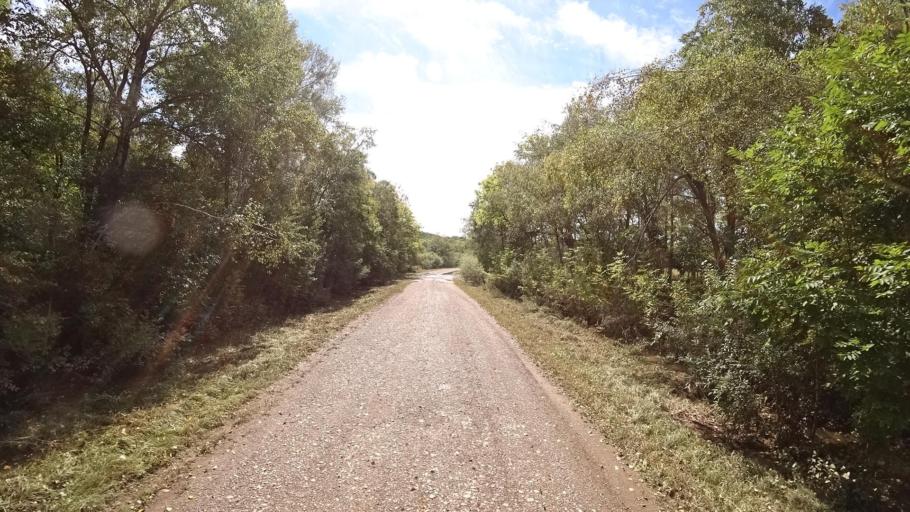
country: RU
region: Primorskiy
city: Yakovlevka
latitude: 44.6637
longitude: 133.7505
